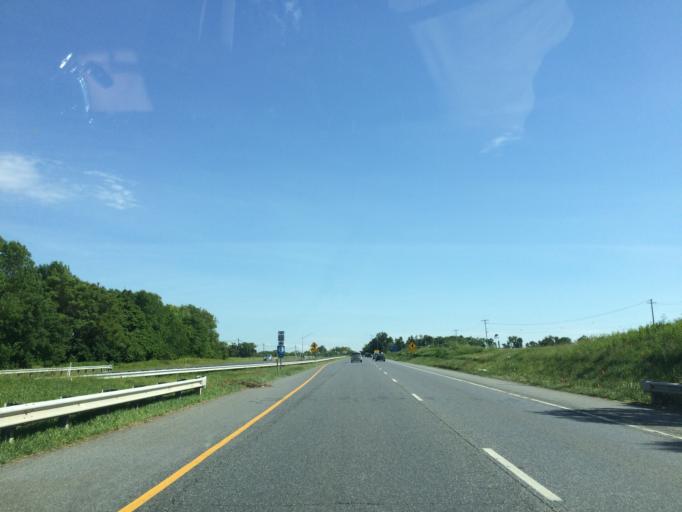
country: US
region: Maryland
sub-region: Frederick County
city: Clover Hill
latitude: 39.4639
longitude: -77.4018
